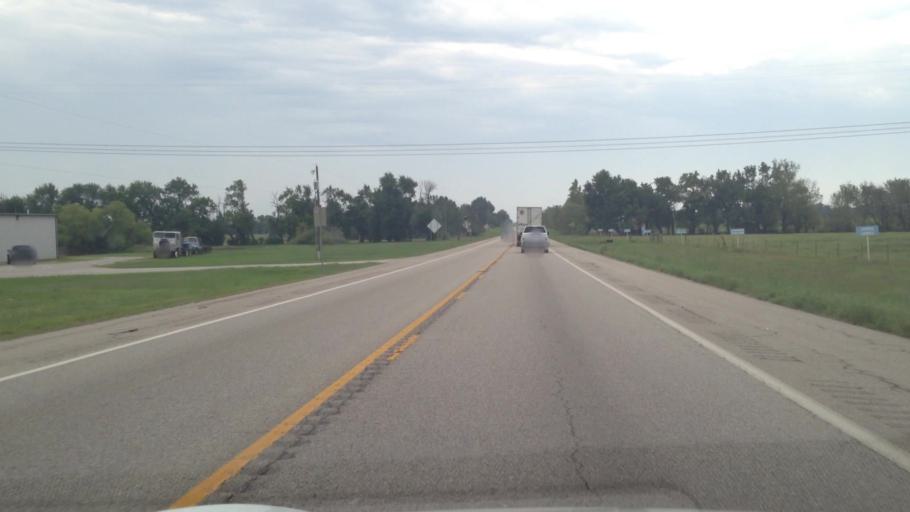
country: US
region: Kansas
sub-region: Crawford County
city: Pittsburg
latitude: 37.3335
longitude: -94.7054
